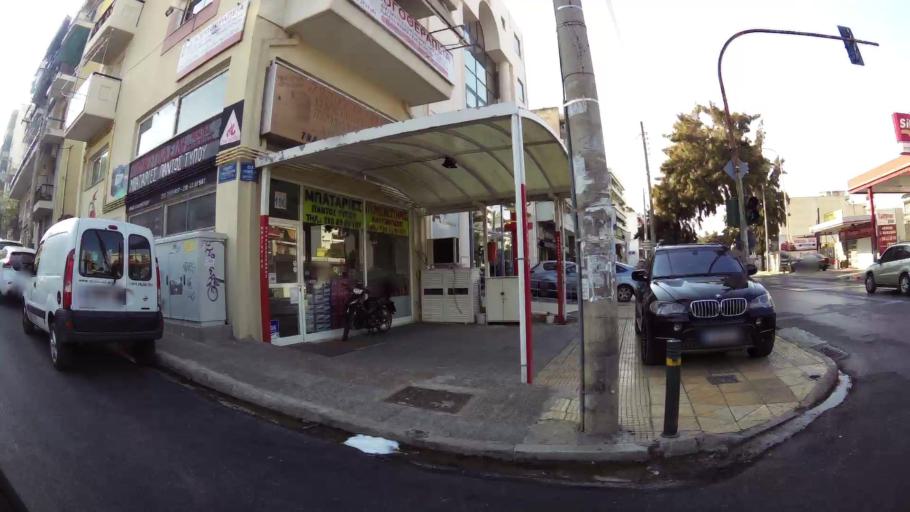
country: GR
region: Attica
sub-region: Nomarchia Athinas
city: Nea Filadelfeia
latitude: 38.0250
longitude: 23.7417
